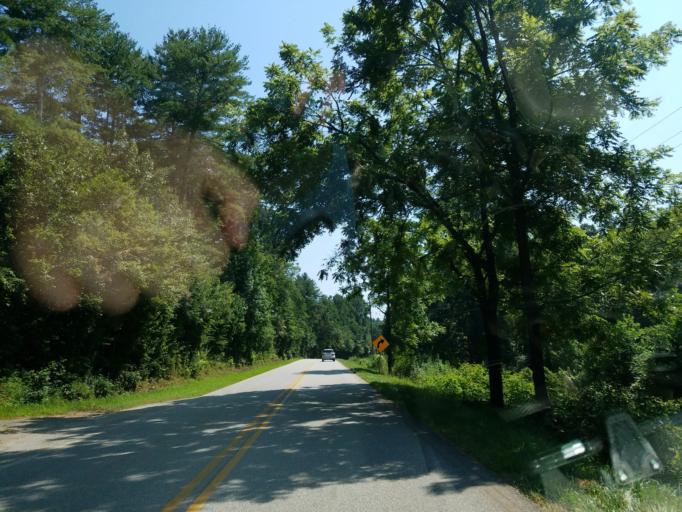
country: US
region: Georgia
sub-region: Lumpkin County
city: Dahlonega
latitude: 34.6531
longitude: -83.9066
